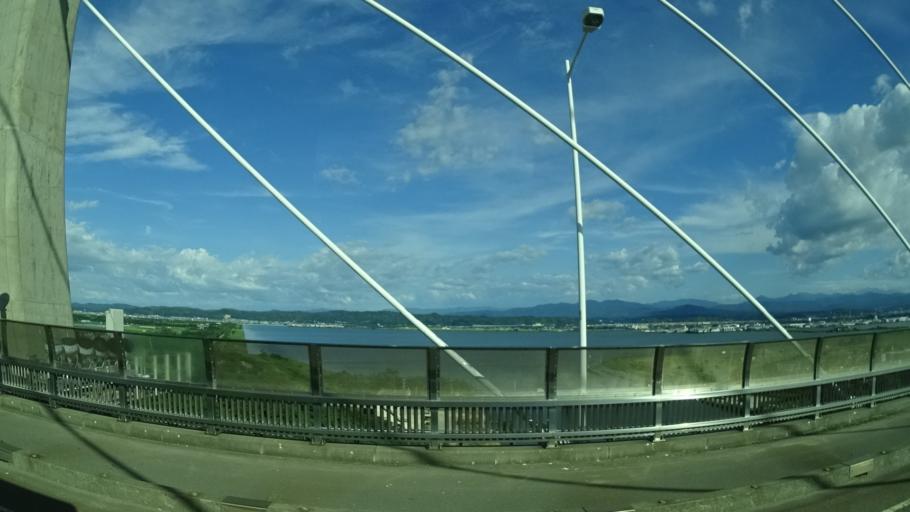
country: JP
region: Ishikawa
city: Kanazawa-shi
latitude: 36.6609
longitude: 136.6513
